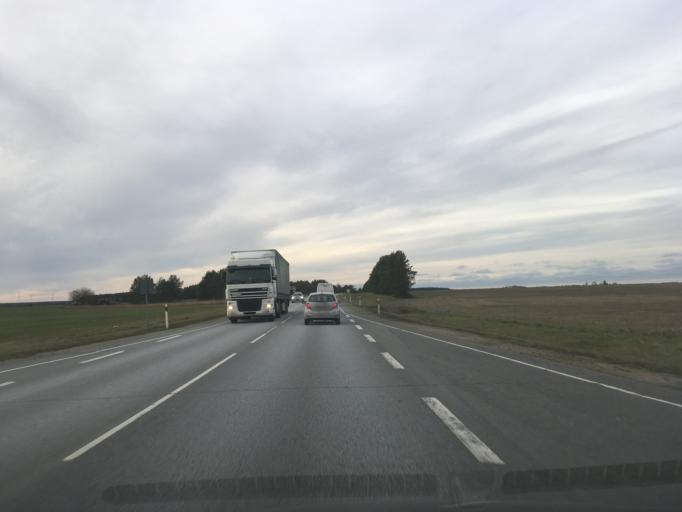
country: EE
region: Ida-Virumaa
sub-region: Puessi linn
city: Pussi
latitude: 59.4038
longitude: 27.0709
